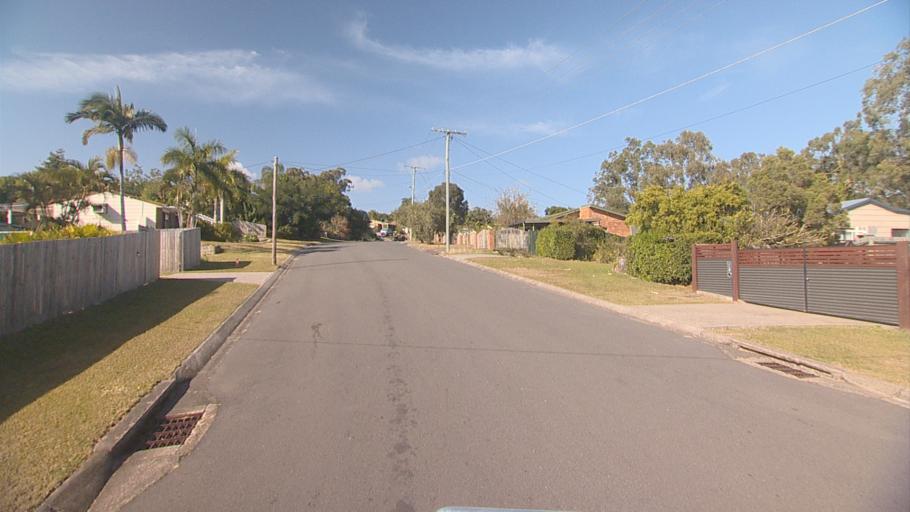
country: AU
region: Queensland
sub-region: Logan
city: Windaroo
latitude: -27.7223
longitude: 153.1836
